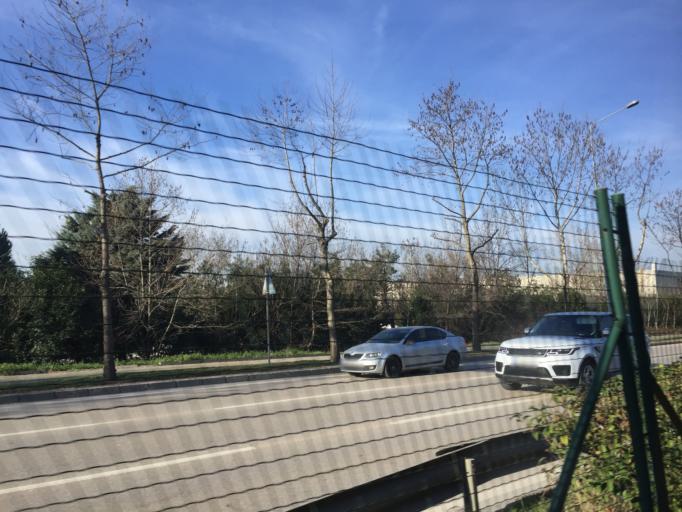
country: TR
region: Bursa
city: Niluefer
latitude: 40.2406
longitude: 28.9707
